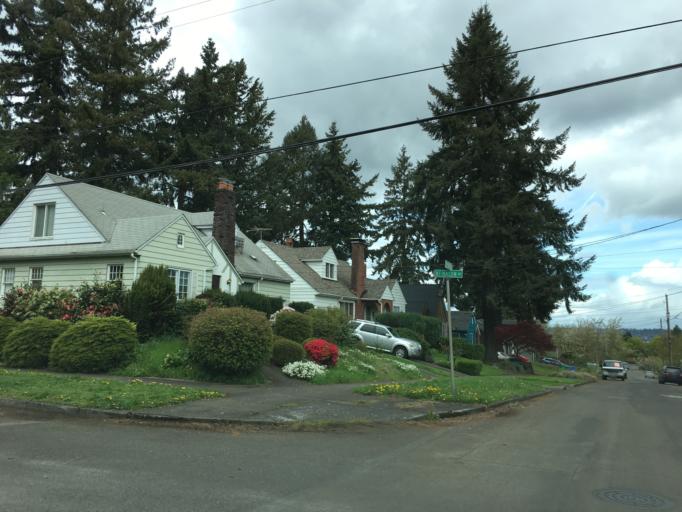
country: US
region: Oregon
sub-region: Multnomah County
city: Lents
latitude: 45.5524
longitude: -122.5838
